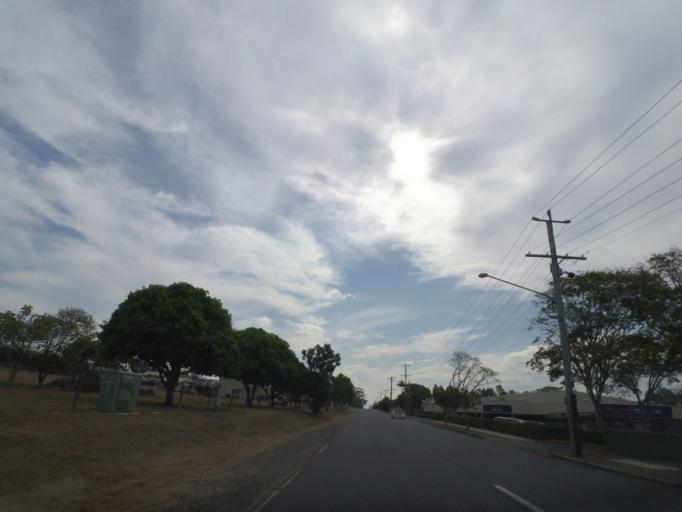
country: AU
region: Queensland
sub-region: Brisbane
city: Richlands
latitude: -27.5920
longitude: 152.9590
